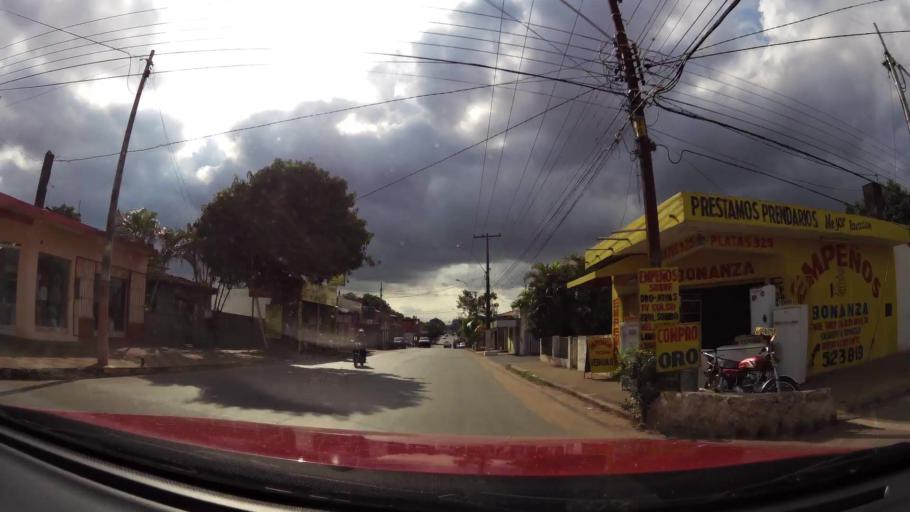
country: PY
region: Central
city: Fernando de la Mora
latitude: -25.3417
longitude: -57.5519
